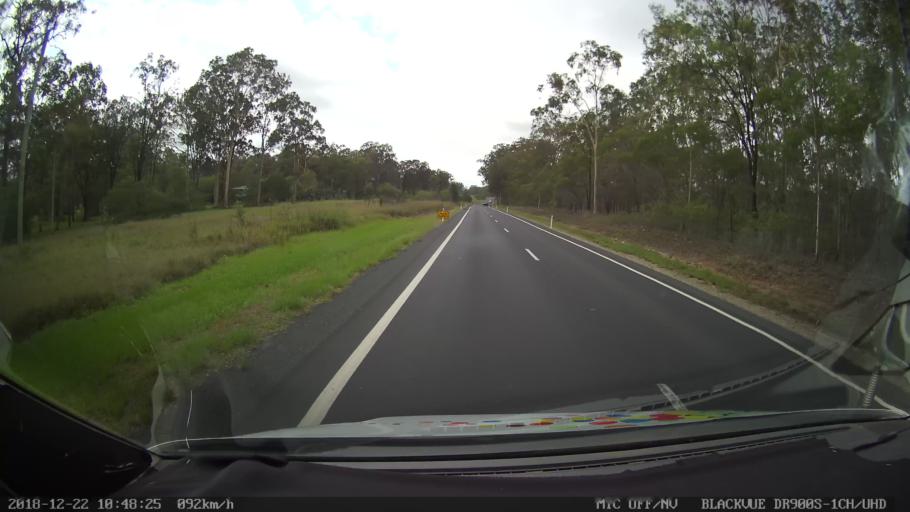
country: AU
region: New South Wales
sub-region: Clarence Valley
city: South Grafton
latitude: -29.6812
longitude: 152.8531
